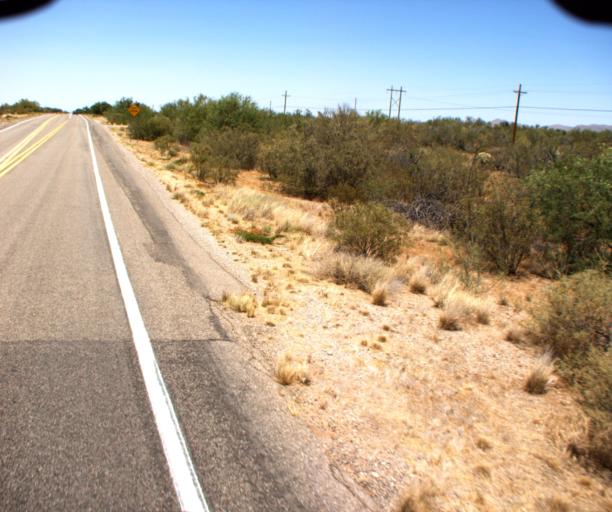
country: US
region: Arizona
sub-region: Pima County
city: Catalina
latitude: 32.7346
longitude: -111.1191
